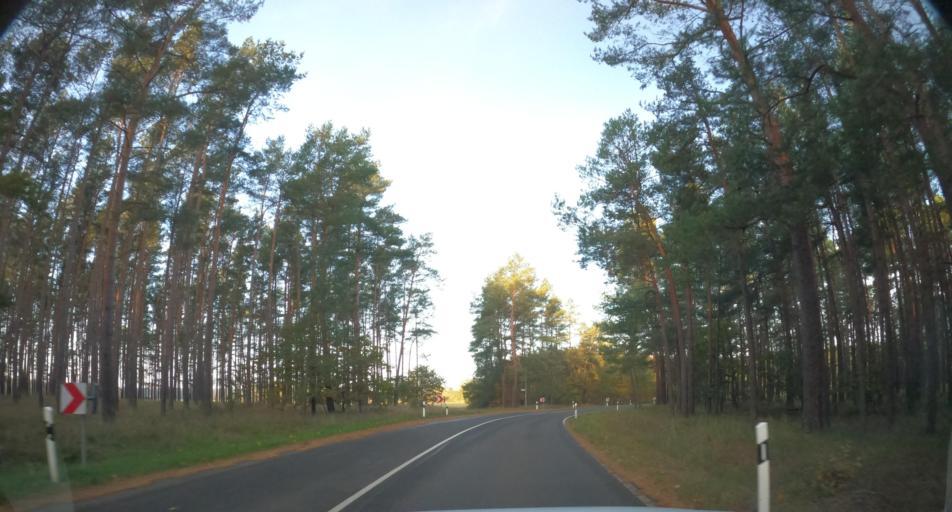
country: DE
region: Mecklenburg-Vorpommern
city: Ahlbeck
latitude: 53.6802
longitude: 14.1769
